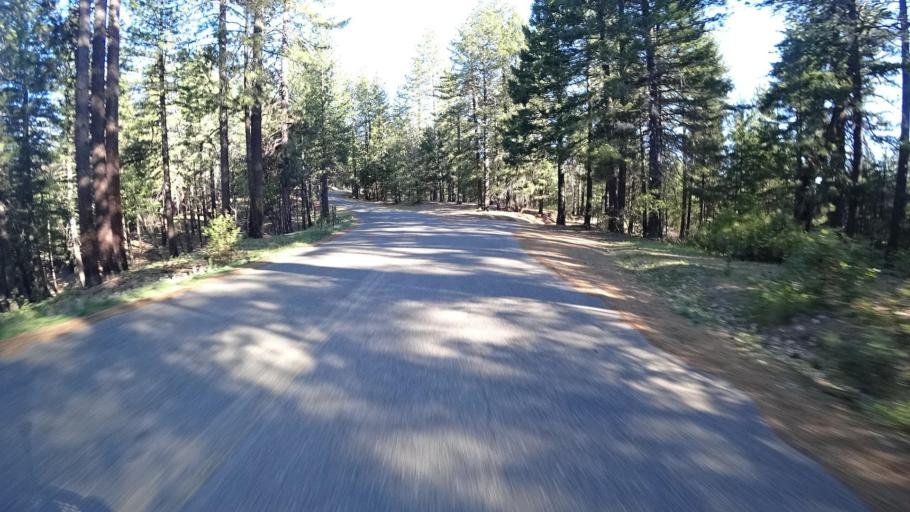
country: US
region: California
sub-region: Lake County
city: Upper Lake
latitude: 39.3037
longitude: -122.9334
